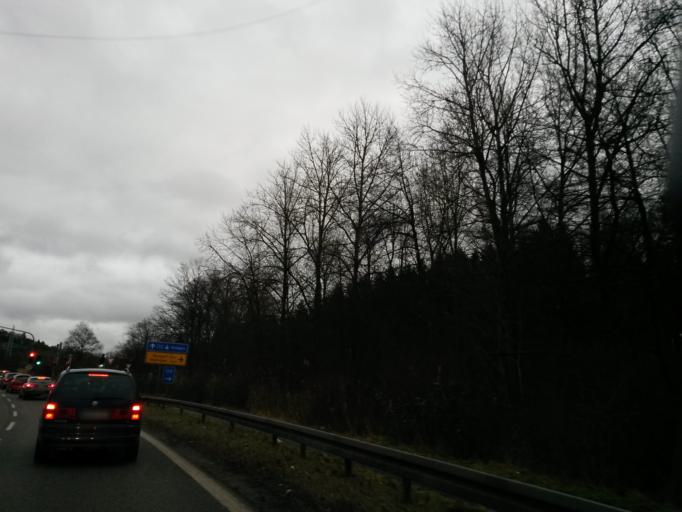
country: DE
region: Baden-Wuerttemberg
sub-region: Regierungsbezirk Stuttgart
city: Sindelfingen
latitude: 48.7036
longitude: 9.0453
